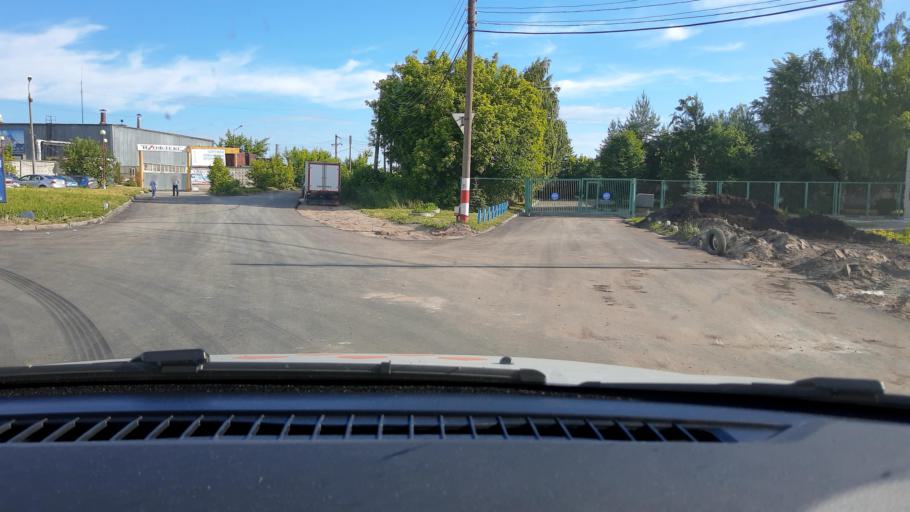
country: RU
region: Nizjnij Novgorod
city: Gorbatovka
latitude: 56.2502
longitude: 43.8324
